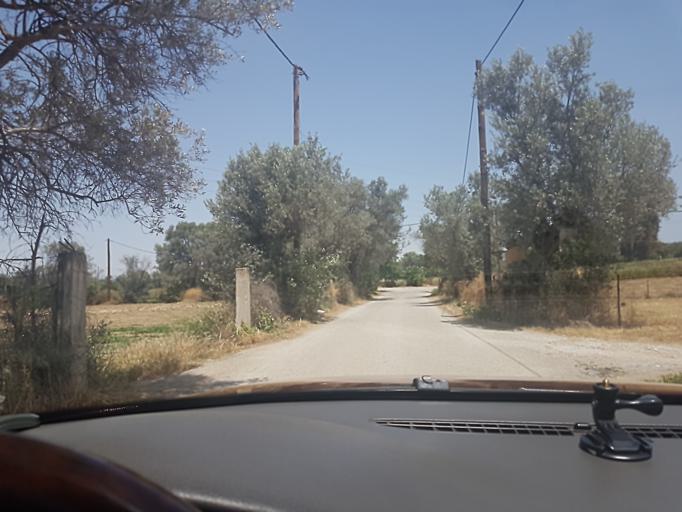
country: GR
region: Central Greece
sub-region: Nomos Evvoias
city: Vasilikon
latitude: 38.4127
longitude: 23.6673
